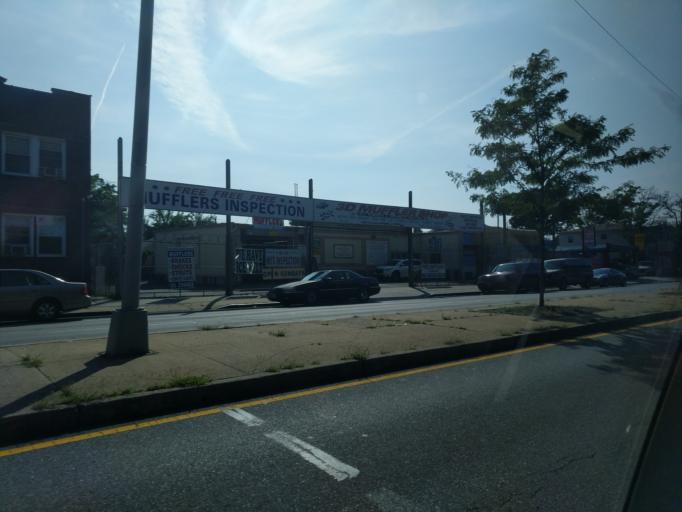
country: US
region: New York
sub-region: Queens County
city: Jamaica
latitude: 40.6846
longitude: -73.7713
